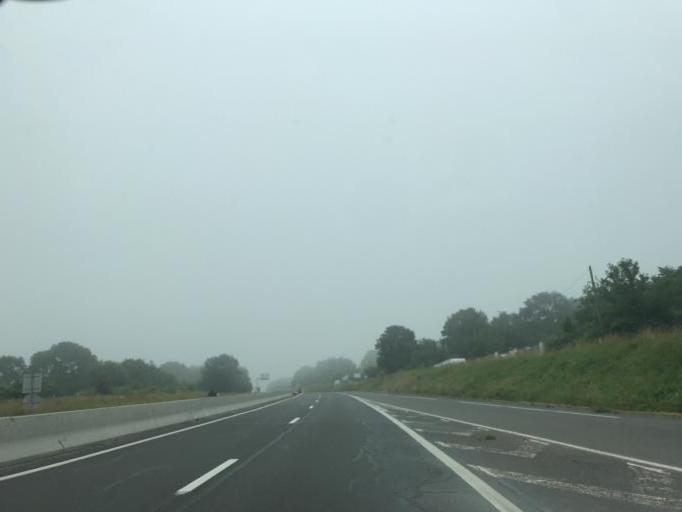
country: FR
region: Ile-de-France
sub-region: Departement de Seine-et-Marne
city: Saint-Thibault-des-Vignes
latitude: 48.8661
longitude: 2.6822
